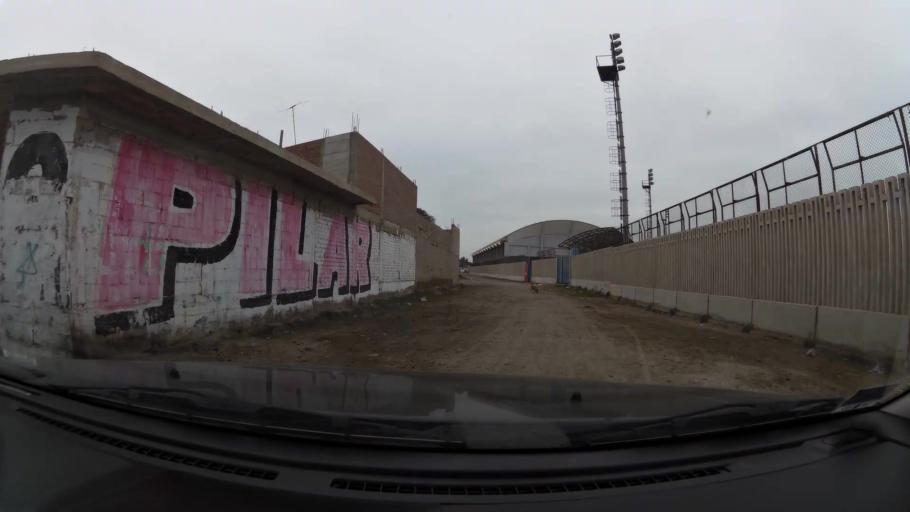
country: PE
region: Ica
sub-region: Provincia de Pisco
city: Pisco
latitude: -13.7167
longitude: -76.2163
